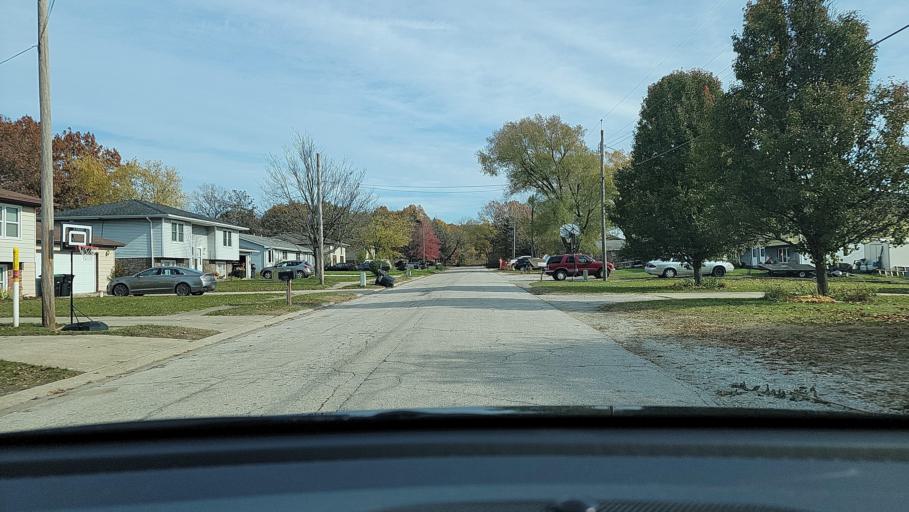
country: US
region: Indiana
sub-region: Lake County
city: Lake Station
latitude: 41.5853
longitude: -87.2098
